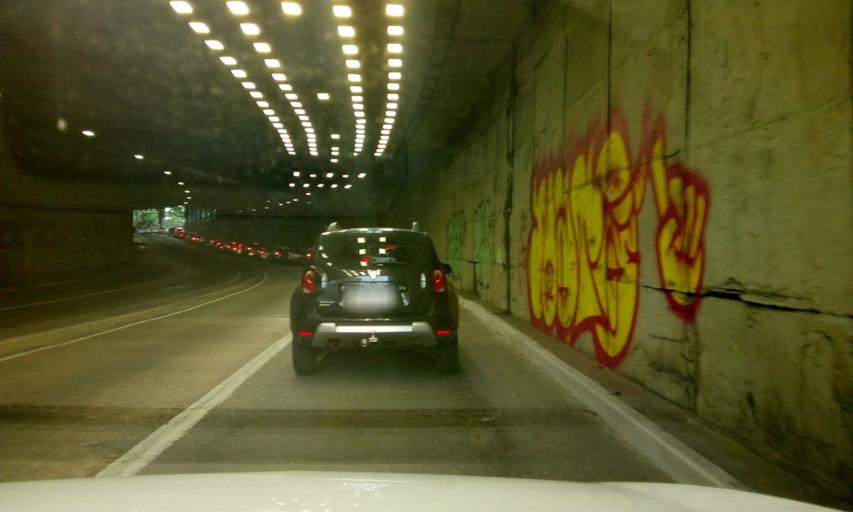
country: BR
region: Sao Paulo
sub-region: Sao Paulo
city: Sao Paulo
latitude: -23.5318
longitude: -46.6639
